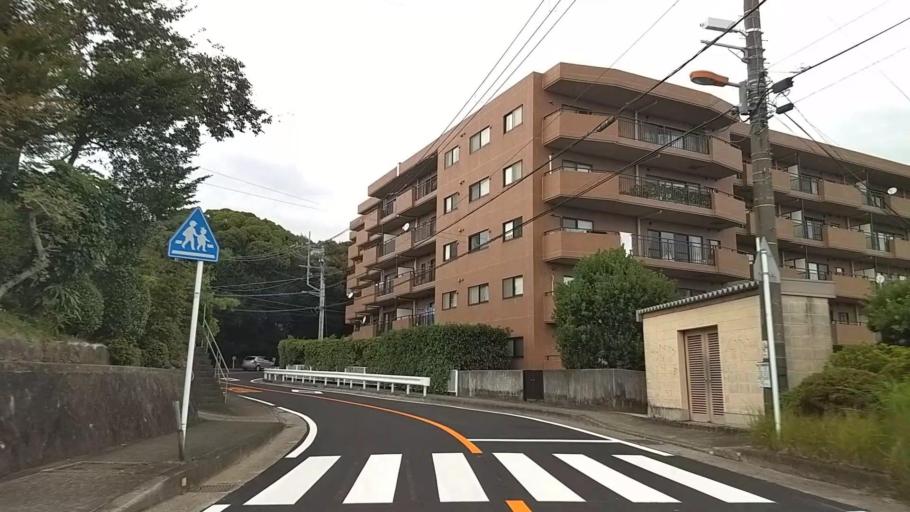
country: JP
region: Kanagawa
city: Yugawara
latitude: 35.1522
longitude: 139.1264
